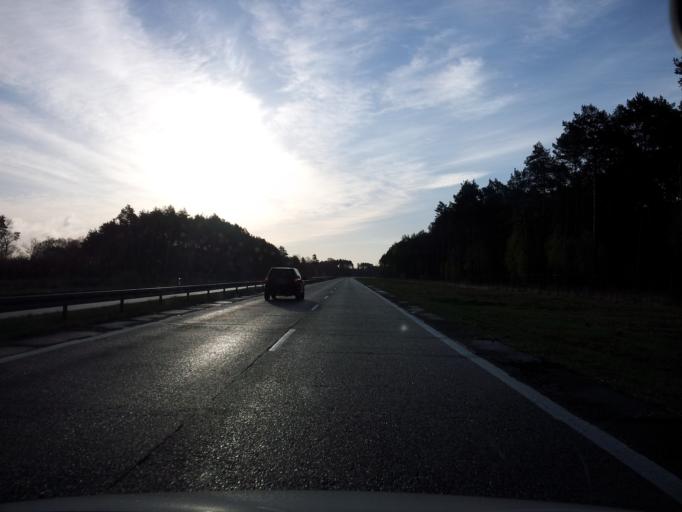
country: PL
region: Lubusz
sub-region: Powiat zarski
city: Lipinki Luzyckie
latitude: 51.6126
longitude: 14.9494
